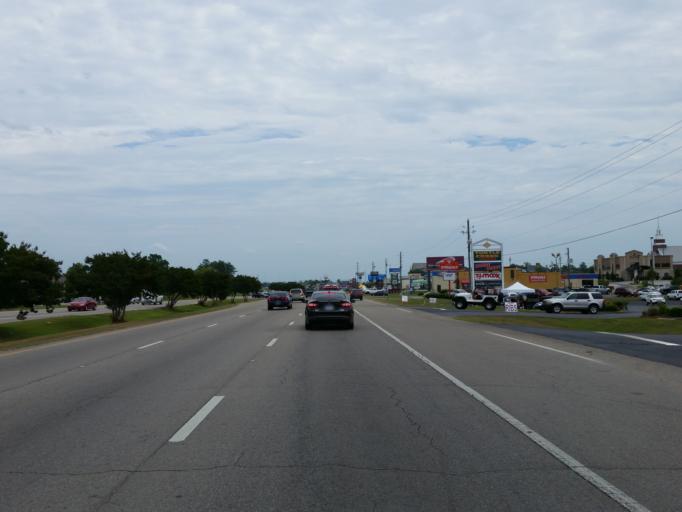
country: US
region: Mississippi
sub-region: Lamar County
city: West Hattiesburg
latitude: 31.3222
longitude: -89.3729
